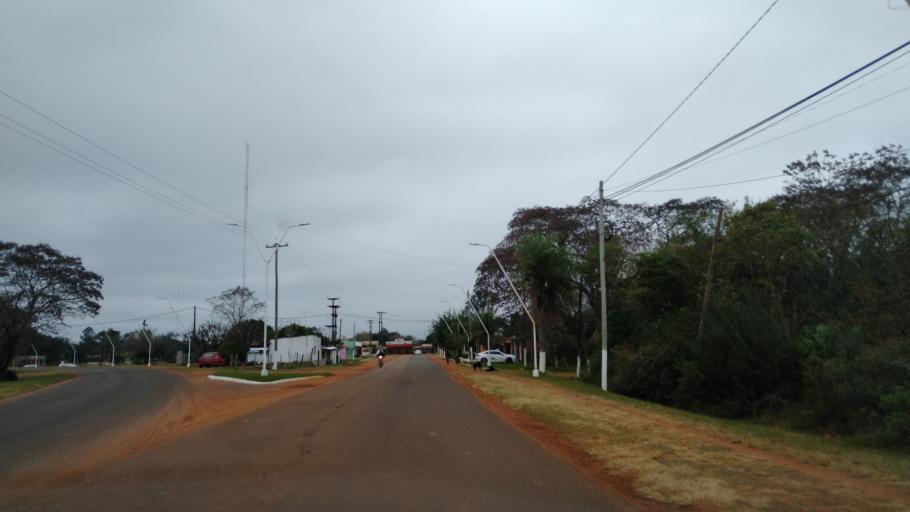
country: AR
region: Corrientes
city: Alvear
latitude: -29.0871
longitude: -56.5494
